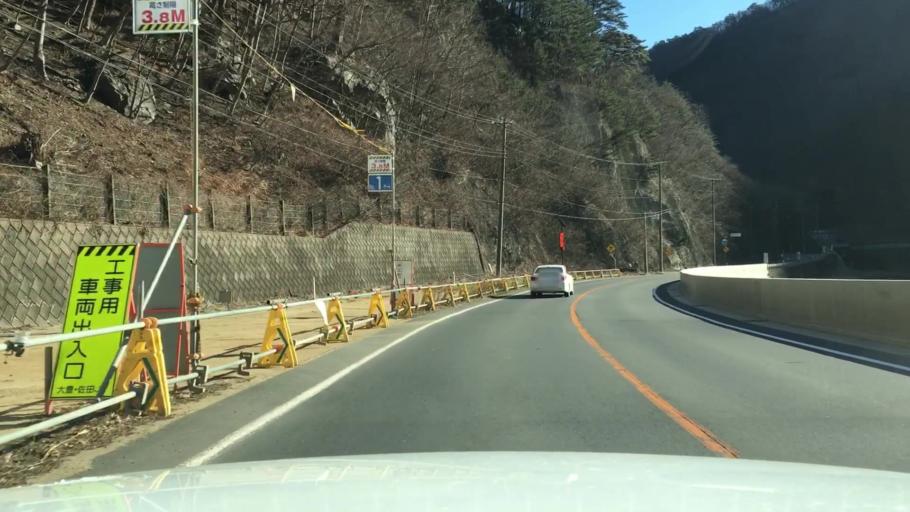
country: JP
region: Iwate
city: Miyako
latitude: 39.5983
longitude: 141.7571
